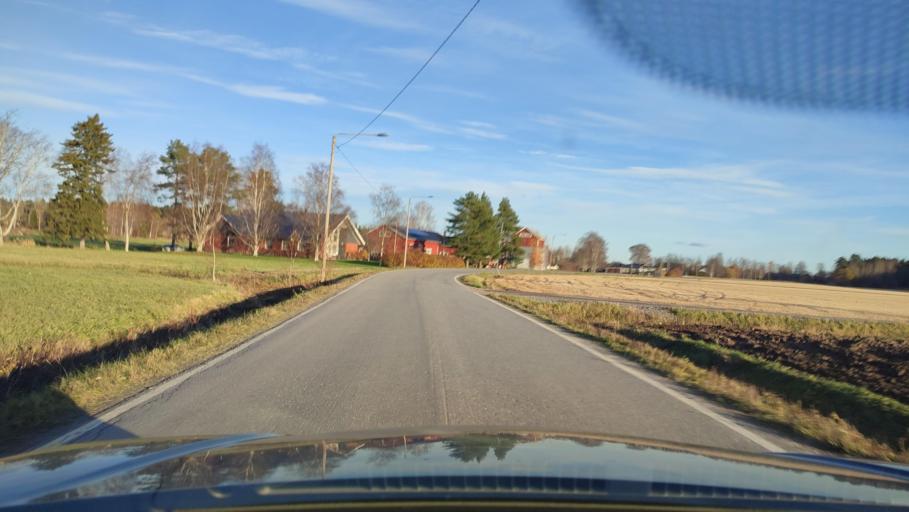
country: FI
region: Ostrobothnia
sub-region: Vaasa
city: Ristinummi
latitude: 62.9983
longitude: 21.7060
